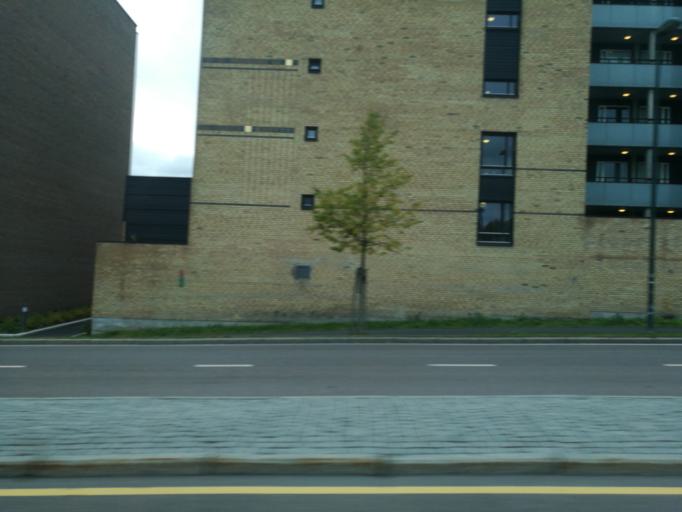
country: NO
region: Akershus
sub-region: Lorenskog
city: Kjenn
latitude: 59.9282
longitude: 10.9509
